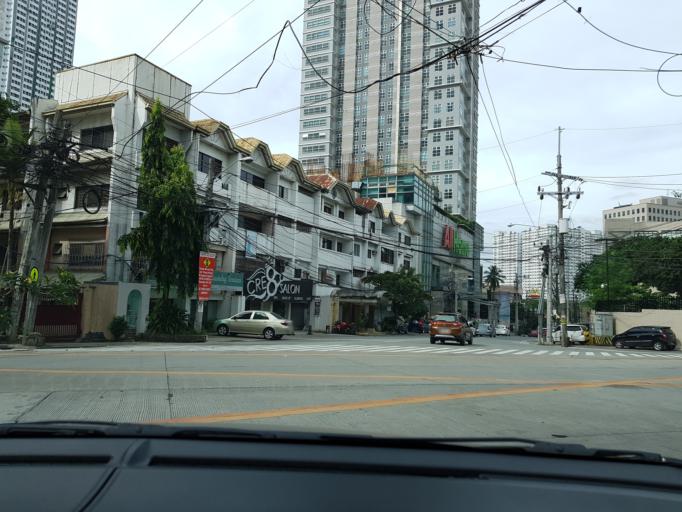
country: PH
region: Metro Manila
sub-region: Quezon City
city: Quezon City
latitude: 14.6385
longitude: 121.0385
